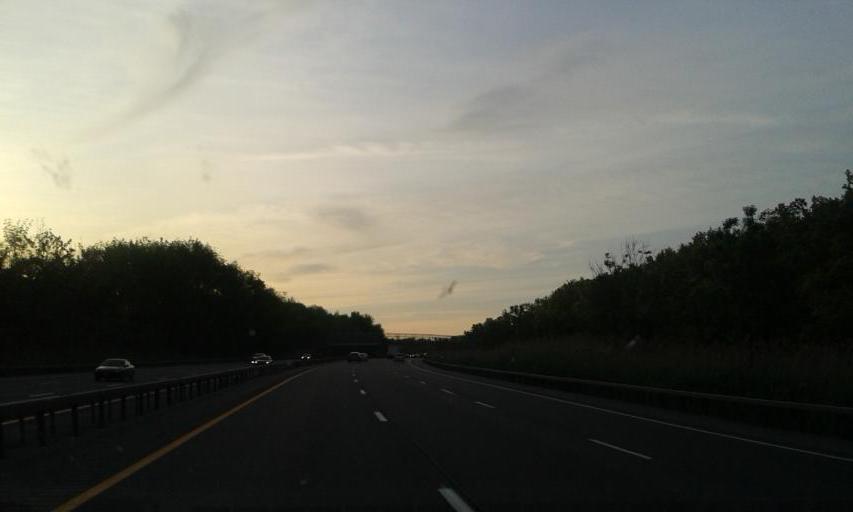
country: US
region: New York
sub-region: Onondaga County
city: Lakeland
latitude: 43.0984
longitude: -76.2407
